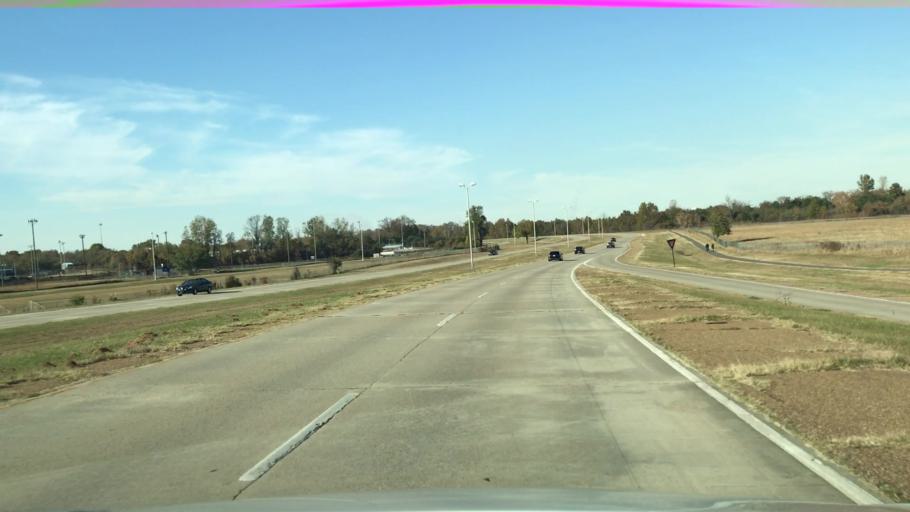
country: US
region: Louisiana
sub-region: Bossier Parish
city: Bossier City
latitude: 32.4787
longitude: -93.6926
